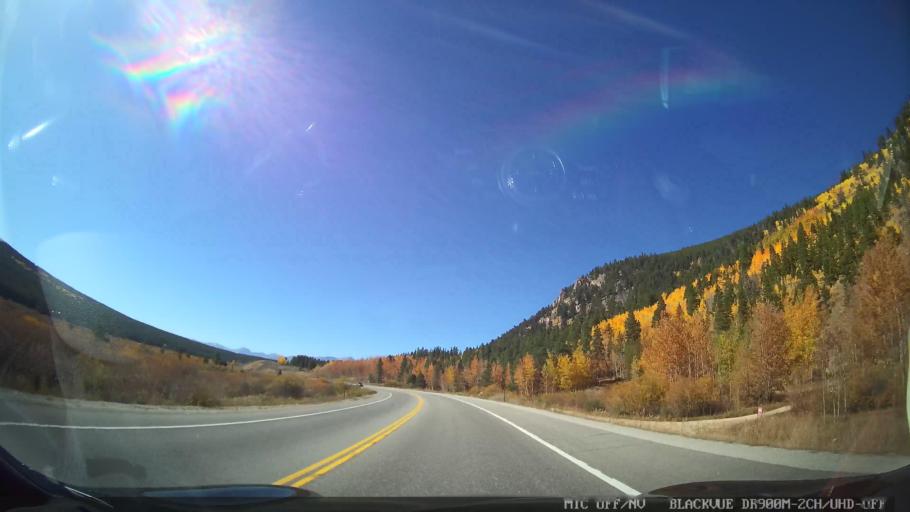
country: US
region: Colorado
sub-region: Lake County
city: Leadville North
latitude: 39.2920
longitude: -106.2782
